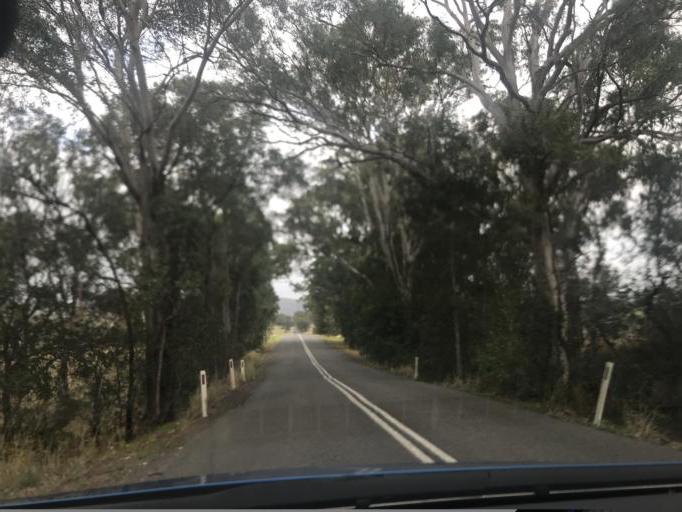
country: AU
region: New South Wales
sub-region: Cessnock
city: Cessnock
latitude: -32.8097
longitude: 151.2960
